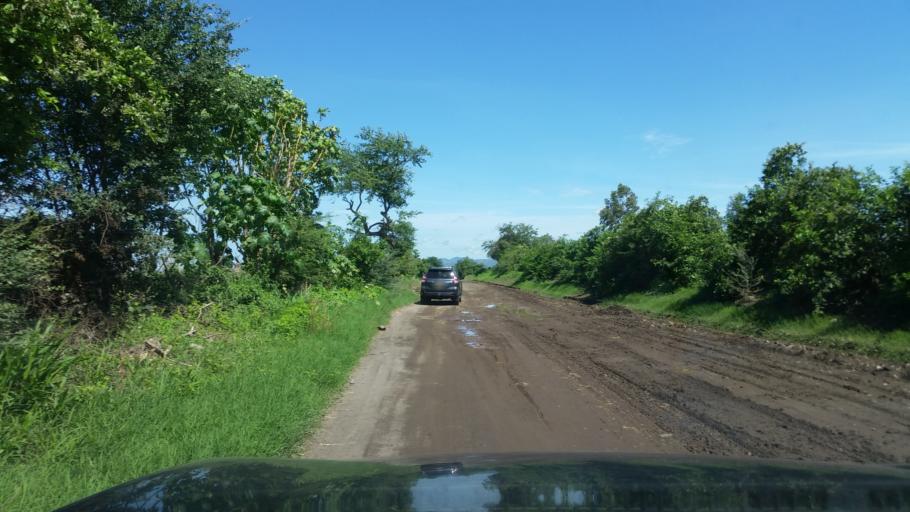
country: NI
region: Chinandega
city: Puerto Morazan
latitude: 12.7721
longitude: -87.0934
